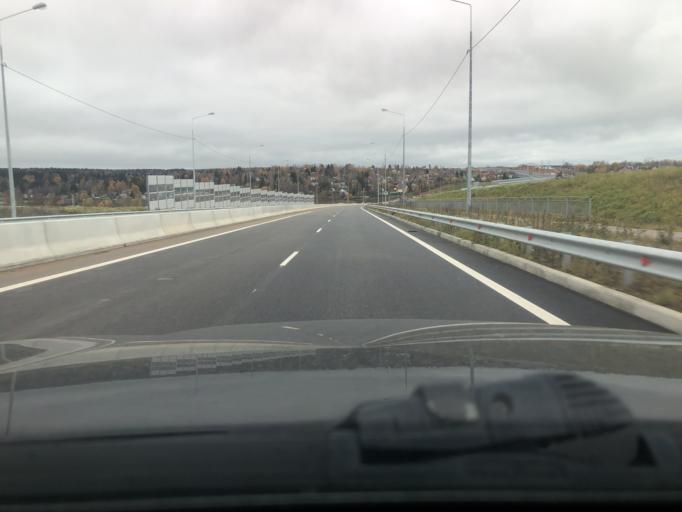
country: RU
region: Moskovskaya
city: Sergiyev Posad
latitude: 56.2967
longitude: 38.1022
